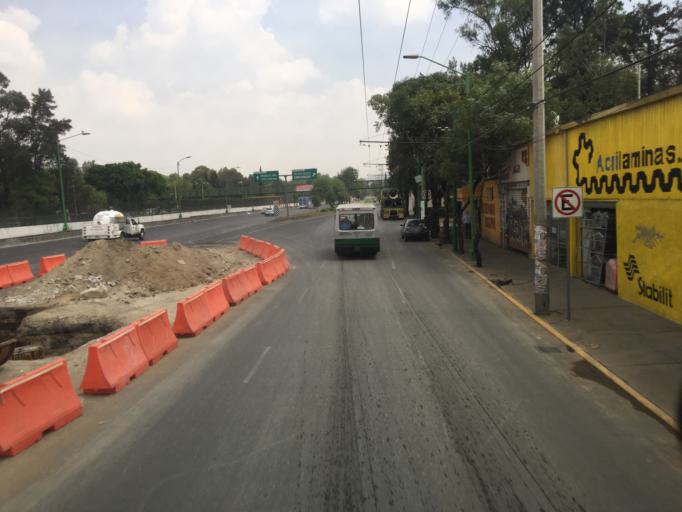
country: MX
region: Mexico
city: Colonia Lindavista
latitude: 19.4950
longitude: -99.1464
